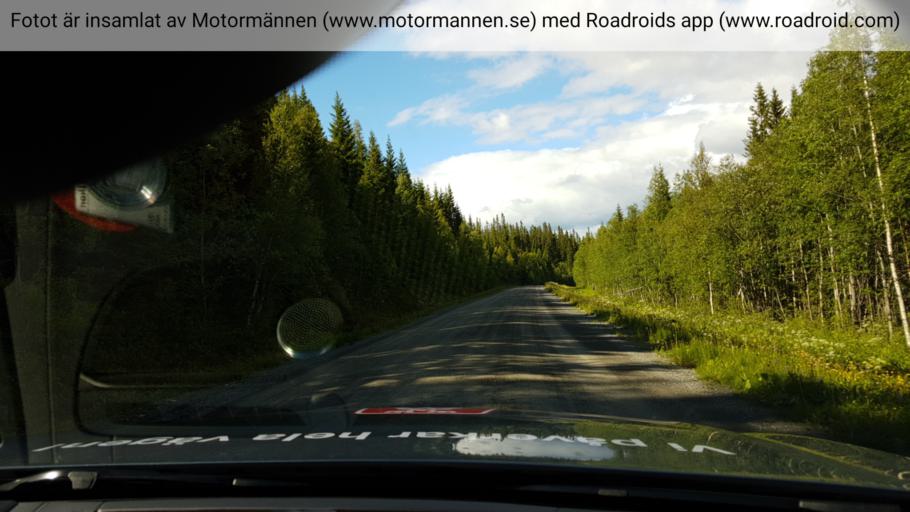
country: SE
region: Jaemtland
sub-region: Krokoms Kommun
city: Valla
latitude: 63.0445
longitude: 13.9598
